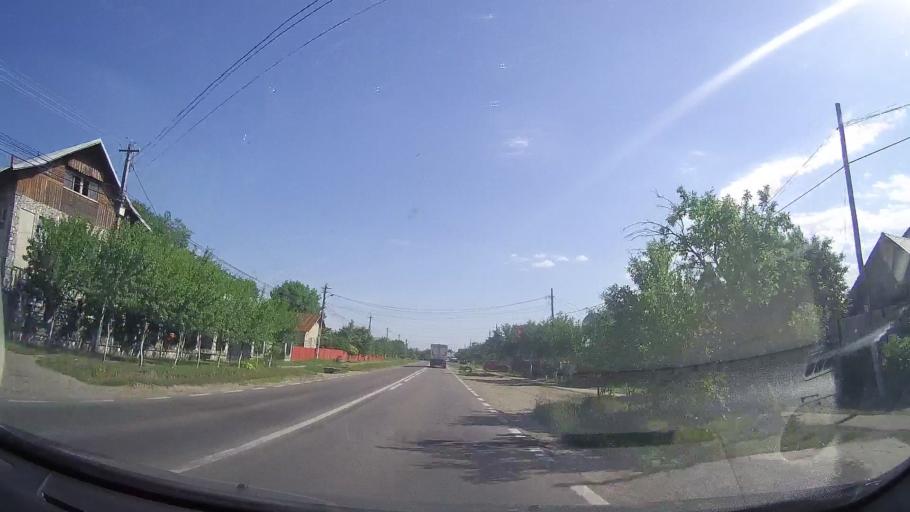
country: RO
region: Prahova
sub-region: Comuna Magurele
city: Magurele
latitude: 45.1205
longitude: 26.0339
